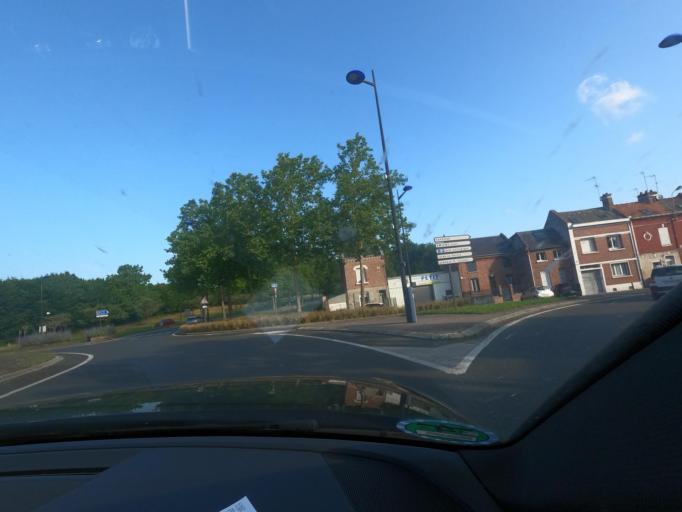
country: FR
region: Picardie
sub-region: Departement de la Somme
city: Pont-de-Metz
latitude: 49.8988
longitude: 2.2665
